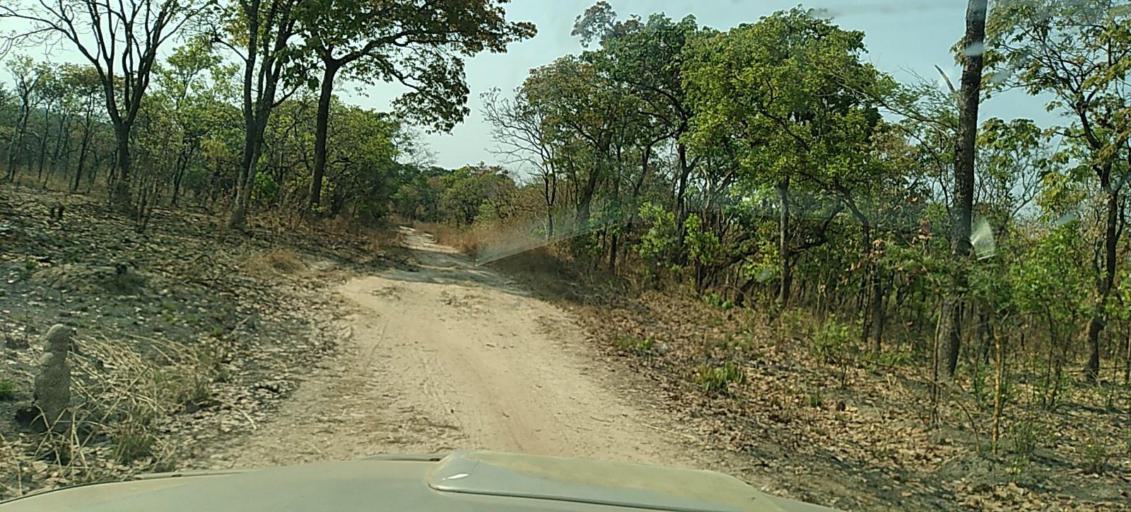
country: ZM
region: North-Western
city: Kasempa
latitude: -13.5373
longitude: 26.4086
